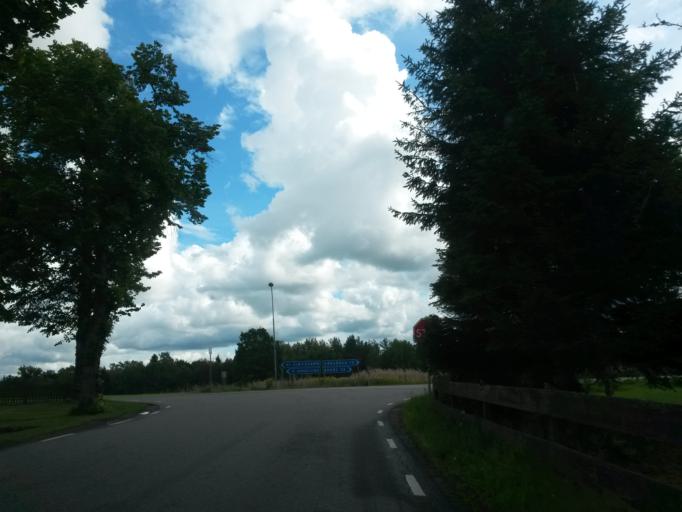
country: SE
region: Vaestra Goetaland
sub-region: Herrljunga Kommun
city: Herrljunga
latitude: 57.9912
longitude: 13.0213
